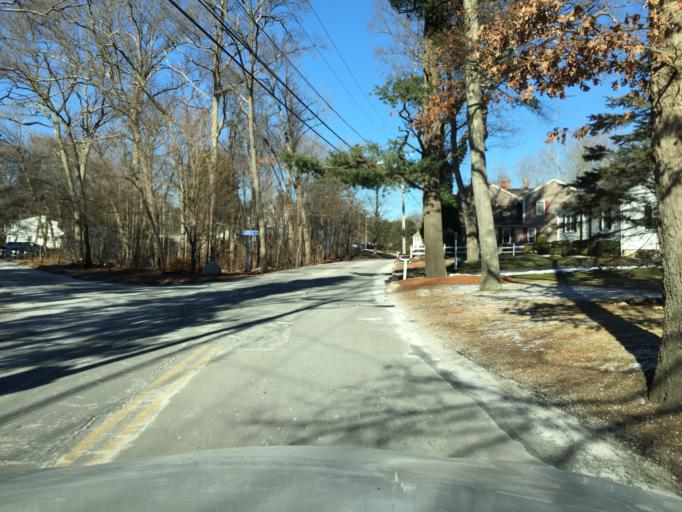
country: US
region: Massachusetts
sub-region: Norfolk County
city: Foxborough
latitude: 42.0614
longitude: -71.2355
